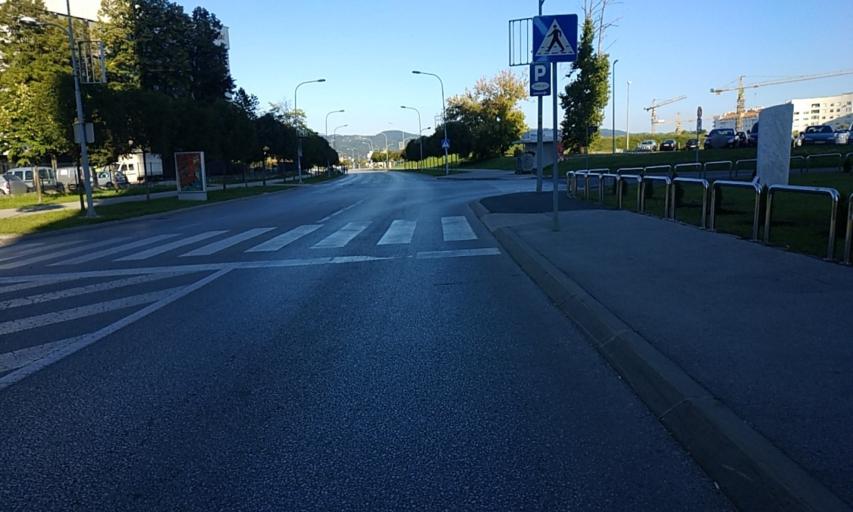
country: BA
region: Republika Srpska
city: Banja Luka
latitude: 44.7784
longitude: 17.1993
